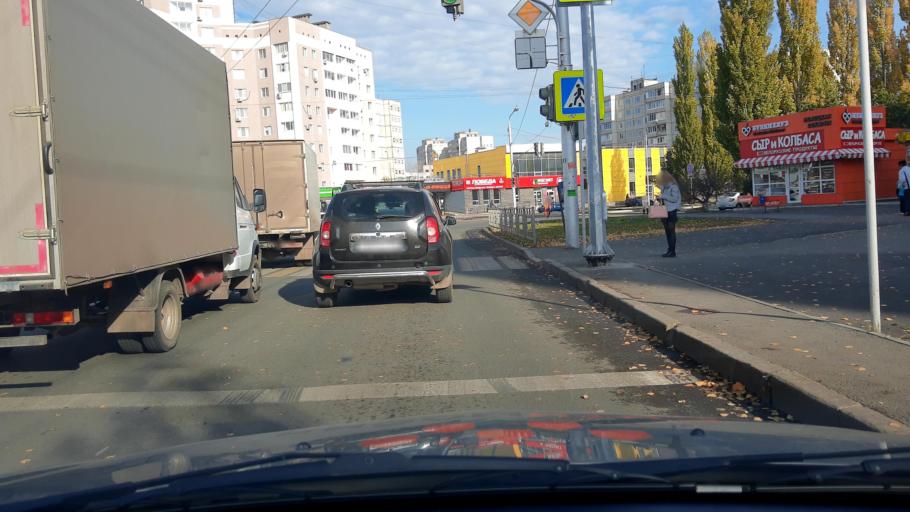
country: RU
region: Bashkortostan
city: Ufa
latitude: 54.7730
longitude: 56.0789
